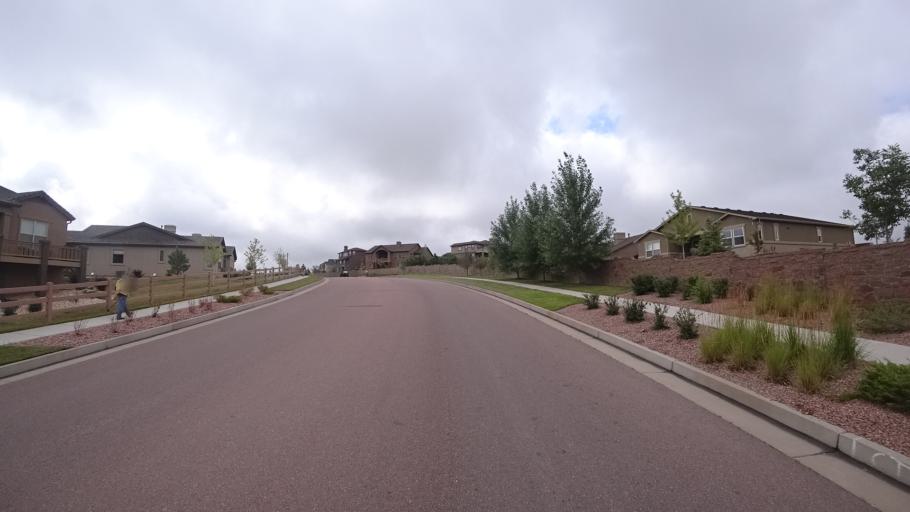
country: US
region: Colorado
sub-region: El Paso County
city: Gleneagle
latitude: 39.0159
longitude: -104.7893
